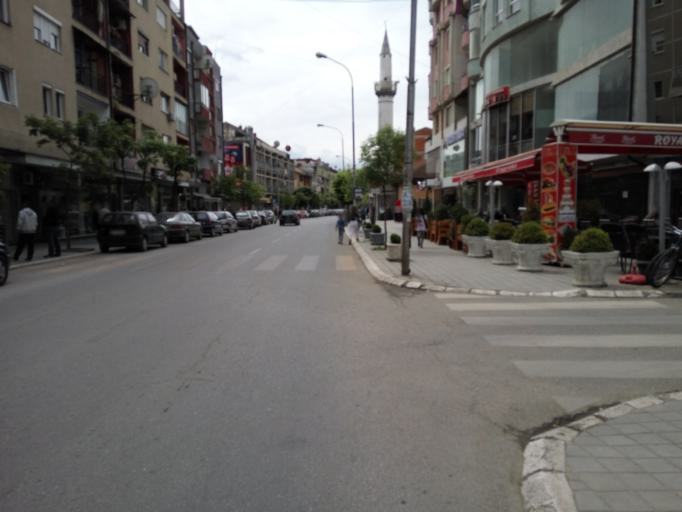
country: XK
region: Gjakova
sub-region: Komuna e Gjakoves
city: Gjakove
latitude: 42.3821
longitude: 20.4307
